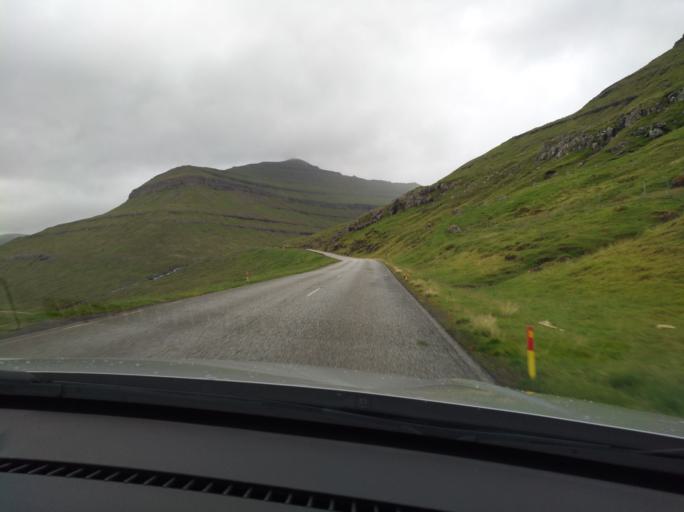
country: FO
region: Eysturoy
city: Fuglafjordur
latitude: 62.2176
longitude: -6.8654
